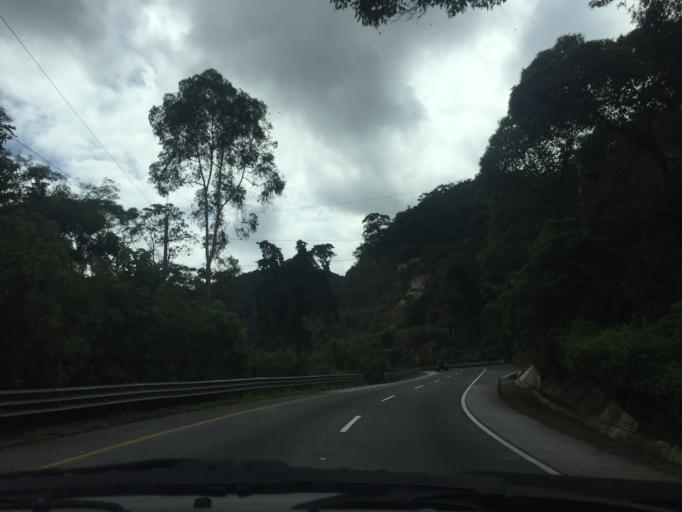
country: GT
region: Sacatepequez
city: Santa Lucia Milpas Altas
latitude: 14.5643
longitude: -90.6970
